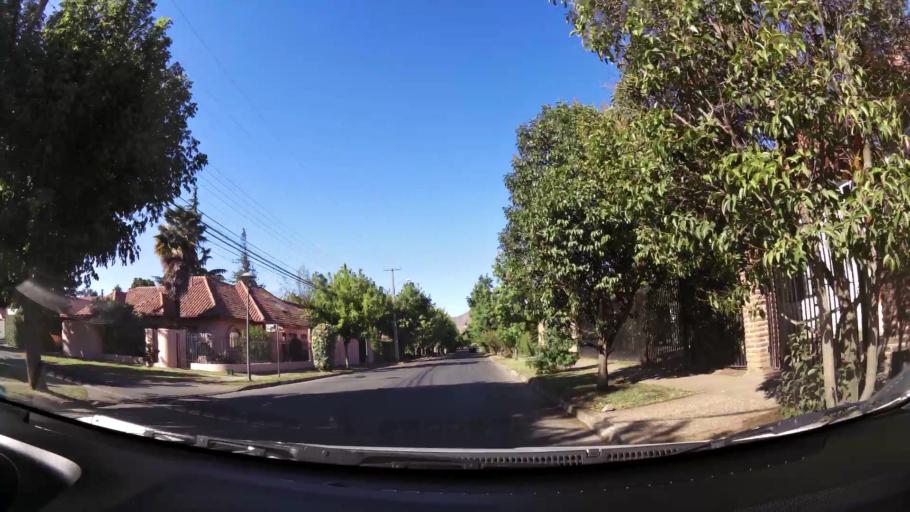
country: CL
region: O'Higgins
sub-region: Provincia de Cachapoal
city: Rancagua
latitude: -34.1899
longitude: -70.7181
